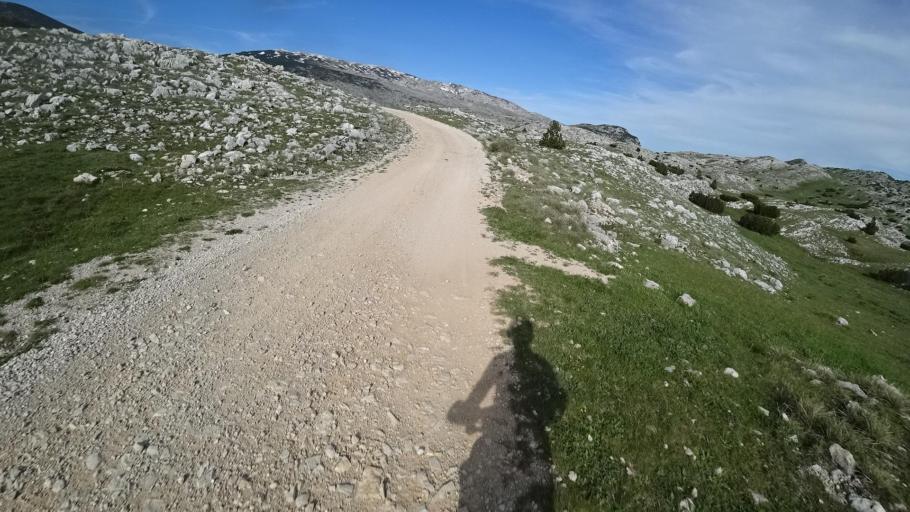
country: BA
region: Federation of Bosnia and Herzegovina
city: Kocerin
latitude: 43.5714
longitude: 17.4961
